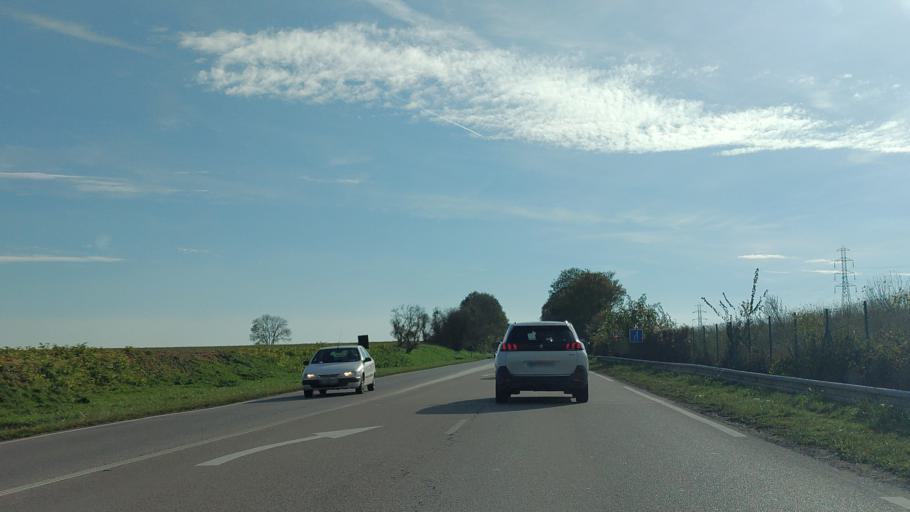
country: FR
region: Ile-de-France
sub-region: Departement du Val-d'Oise
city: Survilliers
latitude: 49.0824
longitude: 2.5296
